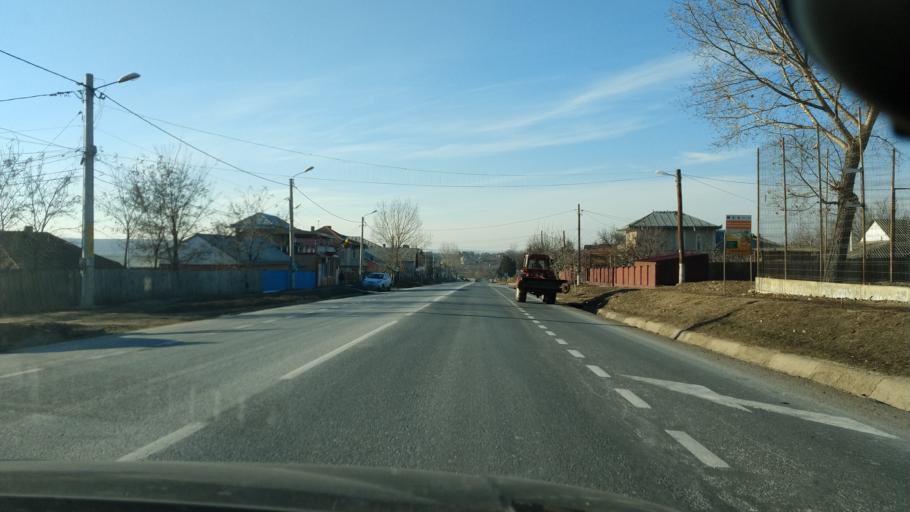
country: RO
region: Iasi
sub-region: Comuna Baltati
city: Baltati
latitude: 47.2201
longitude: 27.1274
